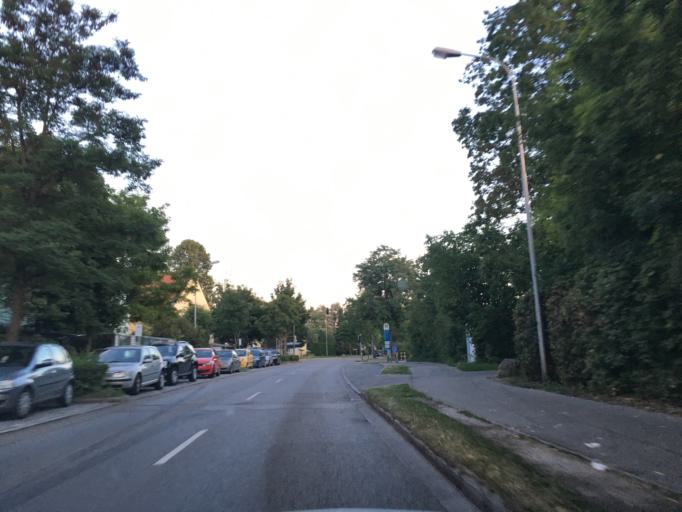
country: DE
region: Bavaria
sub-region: Upper Bavaria
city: Erding
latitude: 48.2958
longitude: 11.9002
